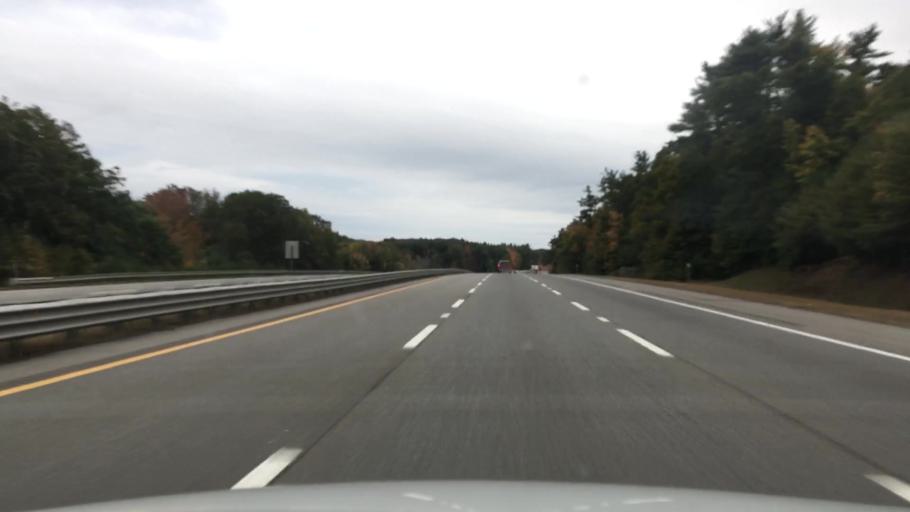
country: US
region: Maine
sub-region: York County
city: Cape Neddick
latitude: 43.1928
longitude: -70.6454
